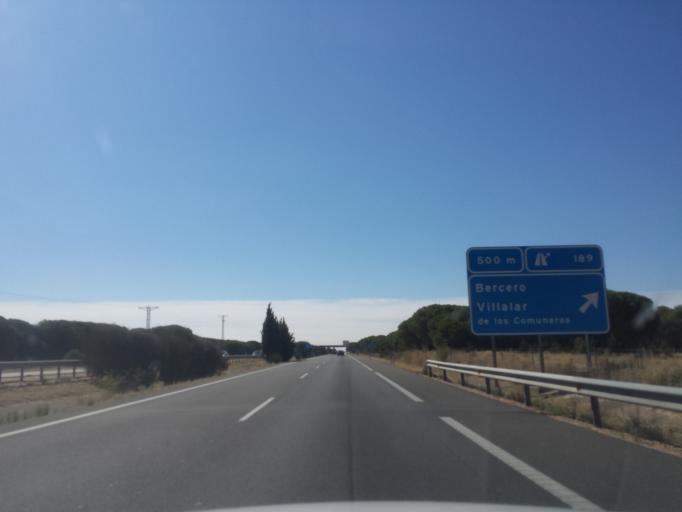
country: ES
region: Castille and Leon
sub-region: Provincia de Valladolid
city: Bercero
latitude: 41.5486
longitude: -5.0747
